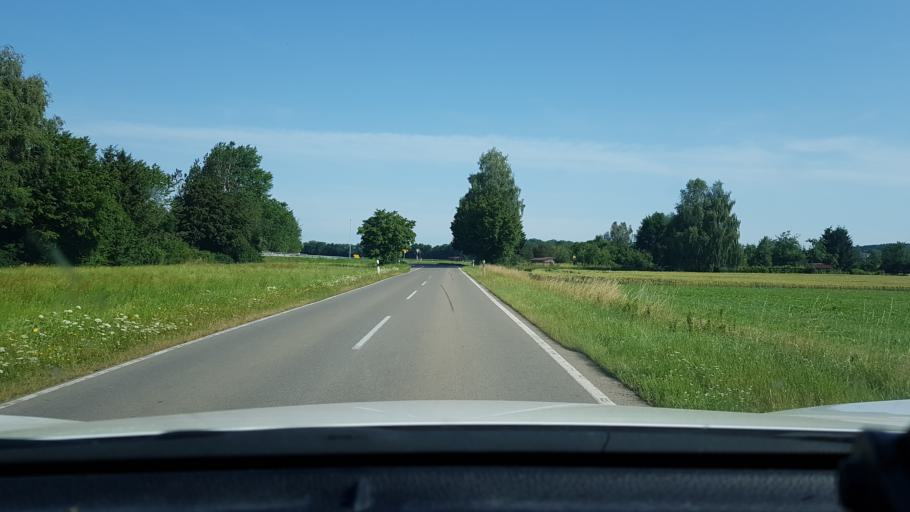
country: DE
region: Baden-Wuerttemberg
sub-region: Tuebingen Region
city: Schwendi
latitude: 48.1993
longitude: 9.9601
